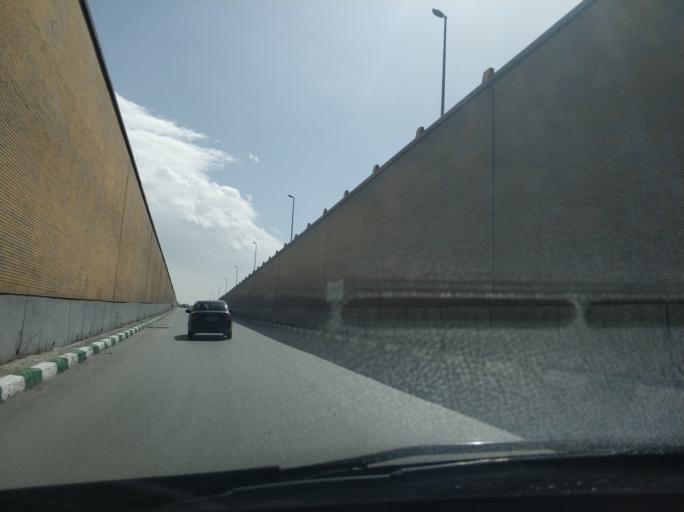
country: IR
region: Razavi Khorasan
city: Torqabeh
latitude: 36.3420
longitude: 59.4542
